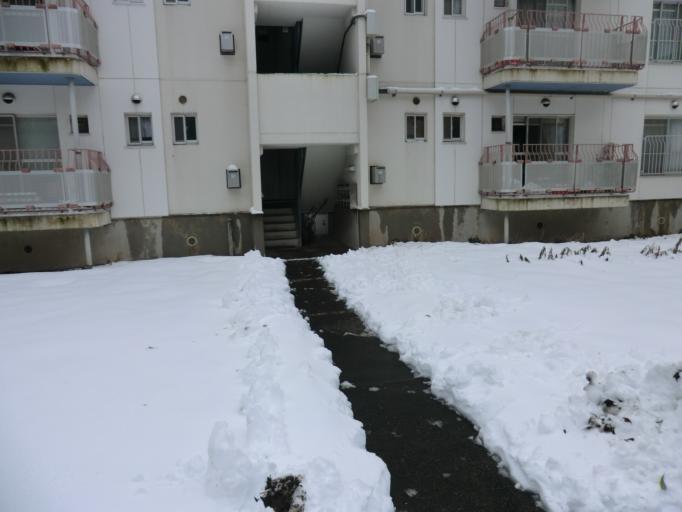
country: JP
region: Ibaraki
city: Naka
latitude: 36.0828
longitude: 140.1075
